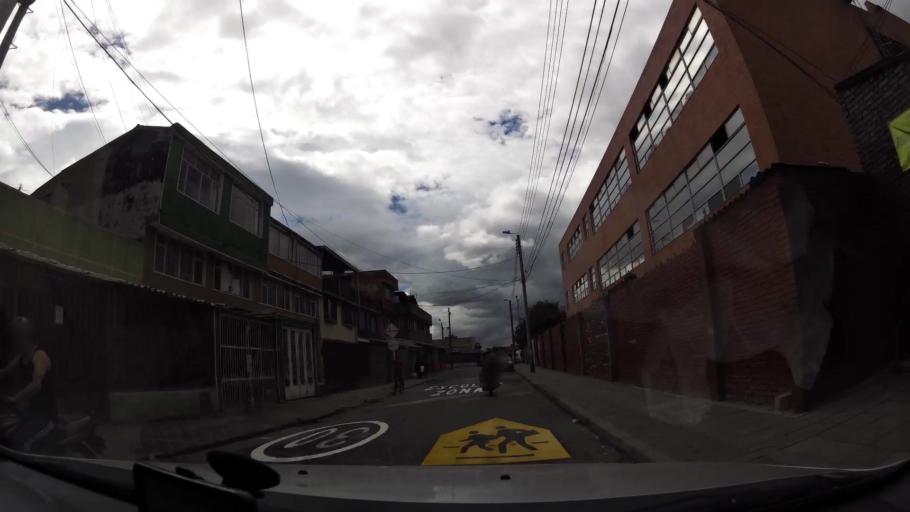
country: CO
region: Bogota D.C.
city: Bogota
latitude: 4.5997
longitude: -74.1344
